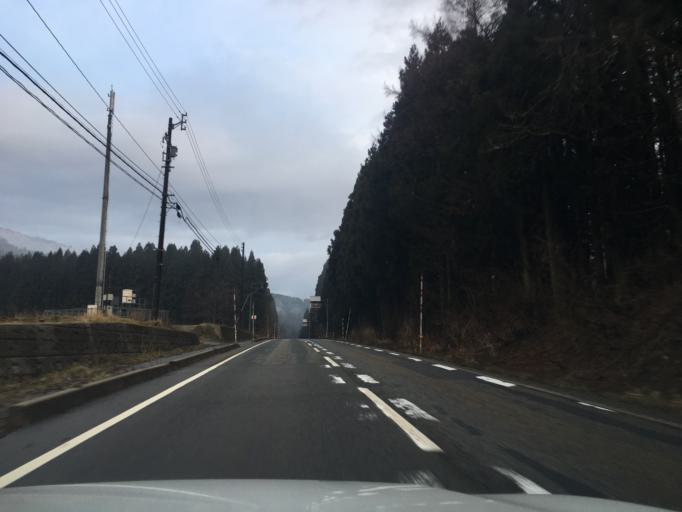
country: JP
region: Niigata
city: Murakami
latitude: 38.3641
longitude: 139.5528
